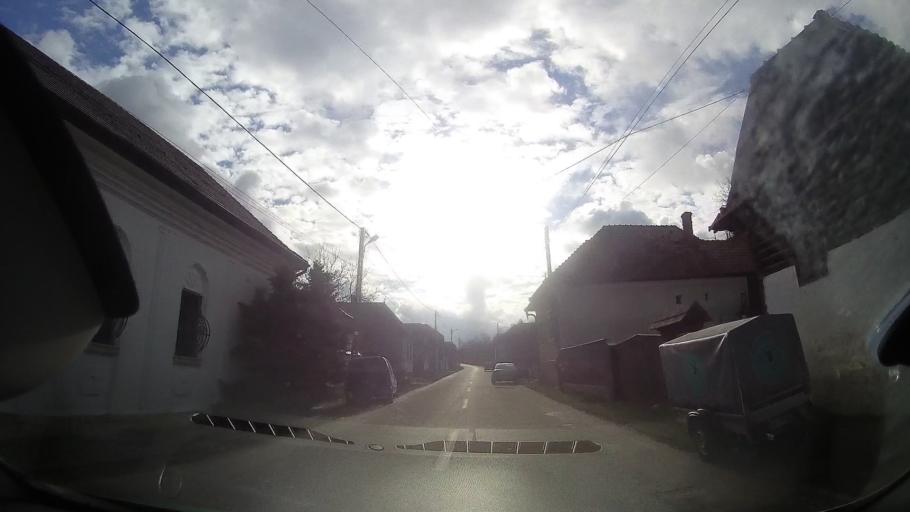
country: RO
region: Alba
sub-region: Comuna Rimetea
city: Rimetea
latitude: 46.4498
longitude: 23.5662
